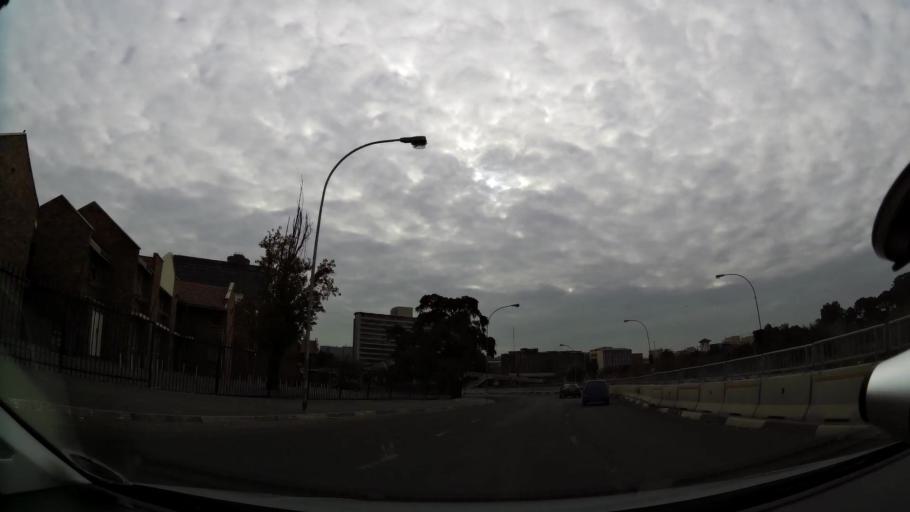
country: ZA
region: Orange Free State
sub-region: Mangaung Metropolitan Municipality
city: Bloemfontein
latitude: -29.1189
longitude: 26.2132
